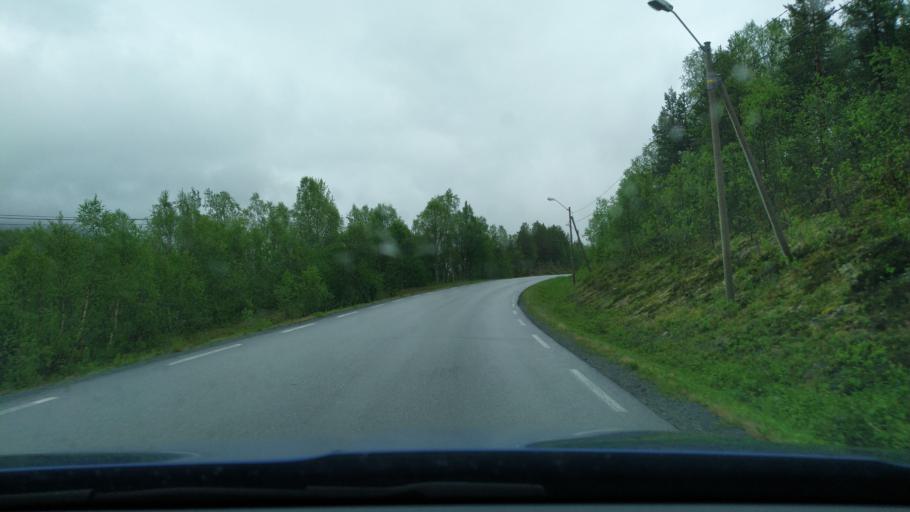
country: NO
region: Troms
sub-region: Dyroy
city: Brostadbotn
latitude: 69.0593
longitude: 17.7337
